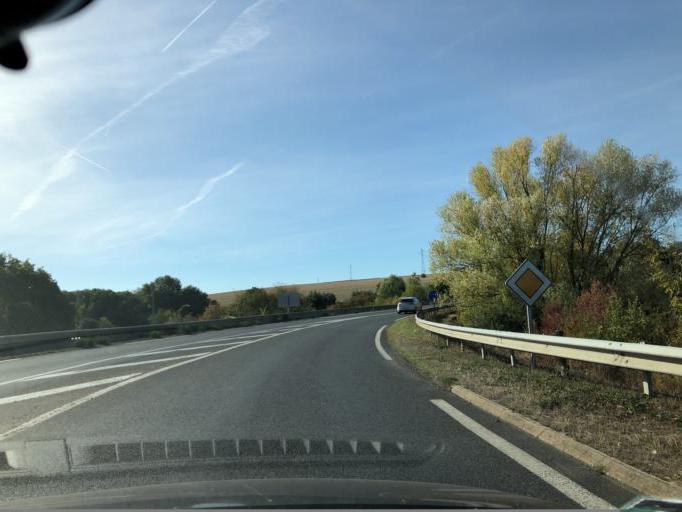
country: FR
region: Ile-de-France
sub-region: Departement de l'Essonne
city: Morigny-Champigny
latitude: 48.4332
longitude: 2.1863
